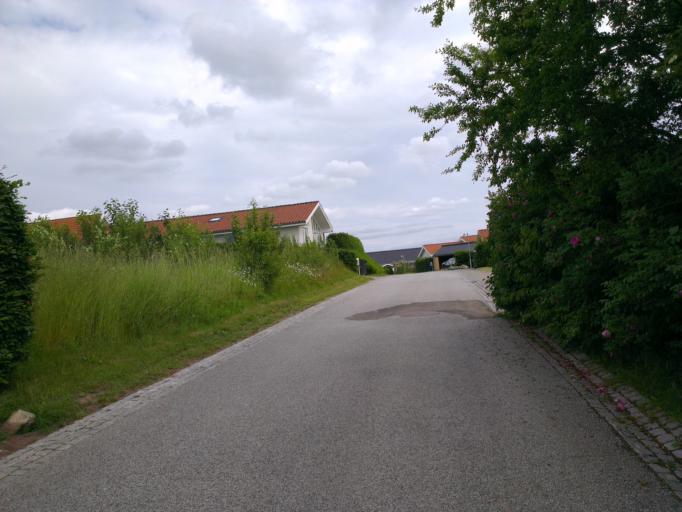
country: DK
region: Capital Region
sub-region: Frederikssund Kommune
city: Frederikssund
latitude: 55.8592
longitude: 12.0715
